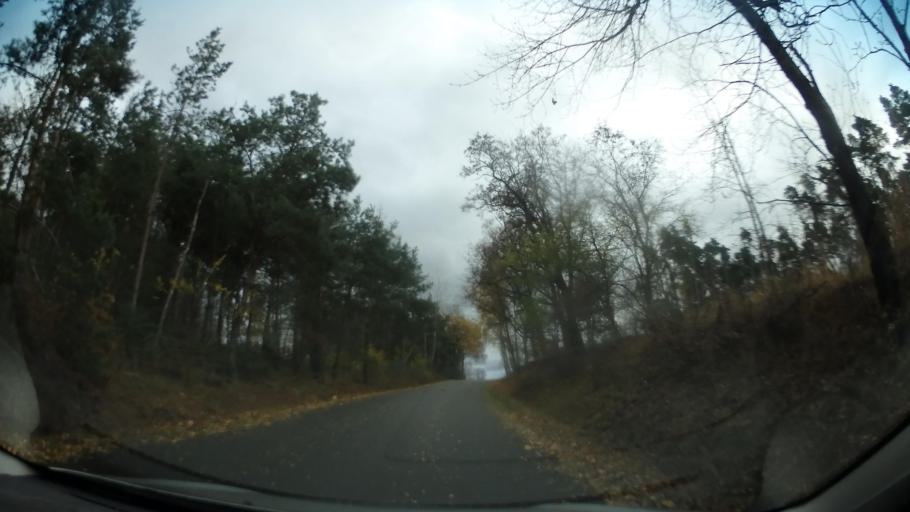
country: CZ
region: Vysocina
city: Namest' nad Oslavou
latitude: 49.2865
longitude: 16.1067
